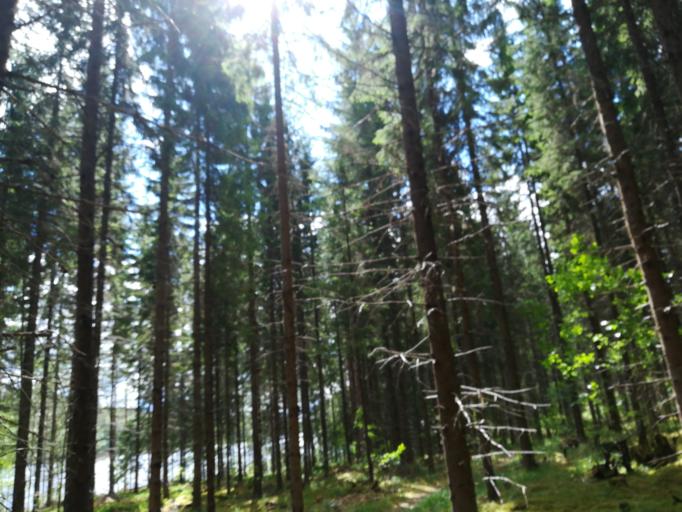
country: FI
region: Southern Savonia
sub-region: Mikkeli
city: Maentyharju
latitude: 61.3645
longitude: 26.9338
